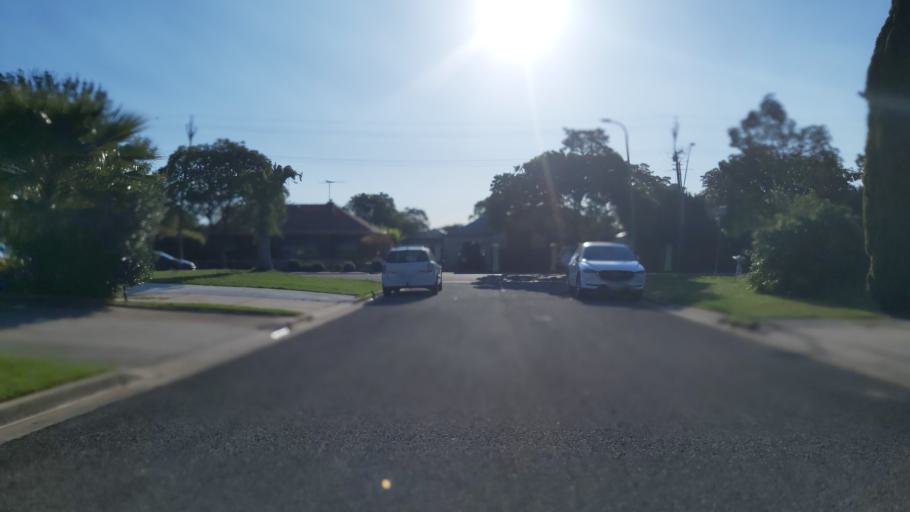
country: AU
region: South Australia
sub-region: Unley
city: Fullarton
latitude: -34.9533
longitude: 138.6222
